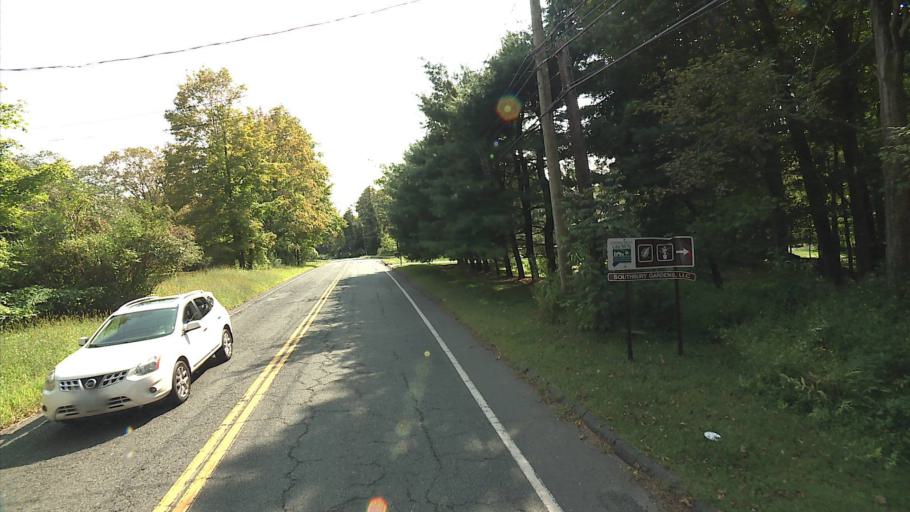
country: US
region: Connecticut
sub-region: New Haven County
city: Heritage Village
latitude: 41.4838
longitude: -73.2578
